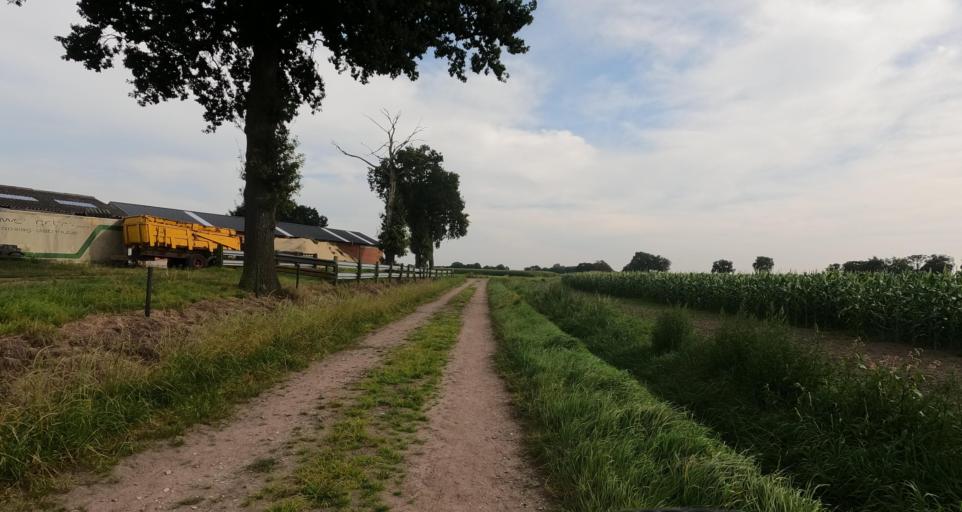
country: BE
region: Flanders
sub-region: Provincie Antwerpen
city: Essen
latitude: 51.4372
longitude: 4.4050
